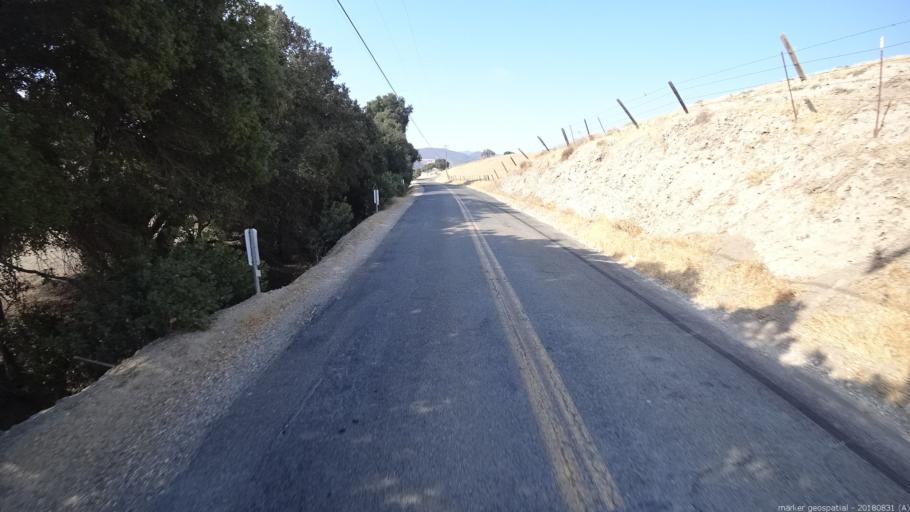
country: US
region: California
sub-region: Monterey County
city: King City
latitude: 36.1725
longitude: -121.1551
